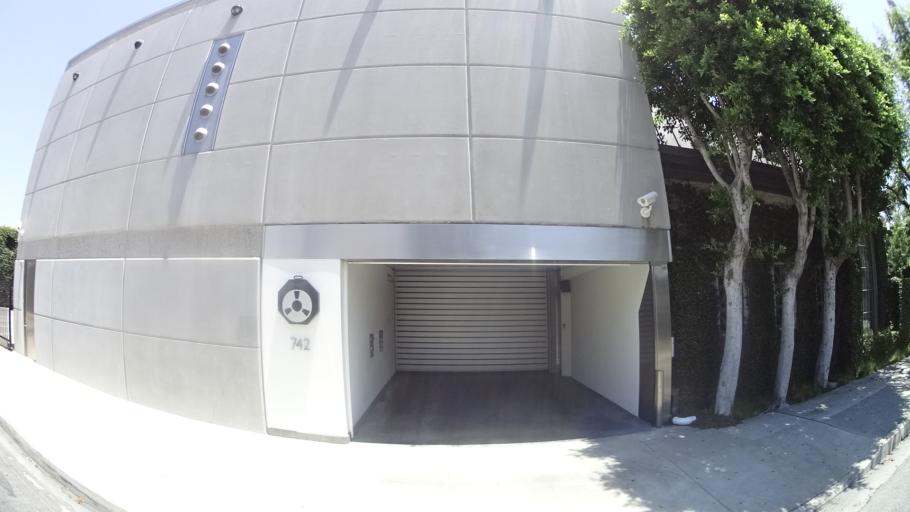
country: US
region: California
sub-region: Los Angeles County
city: Hollywood
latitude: 34.0846
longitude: -118.3332
